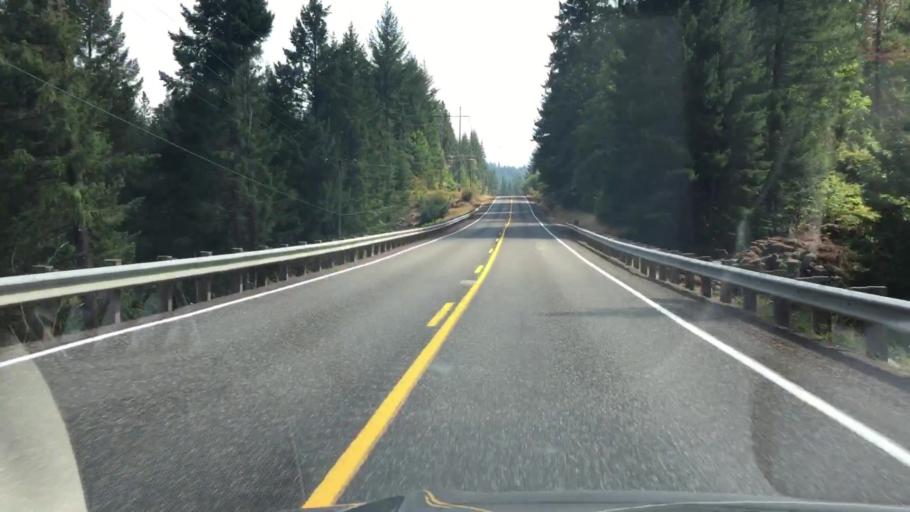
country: US
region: Washington
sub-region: Klickitat County
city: White Salmon
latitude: 45.8717
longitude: -121.5155
